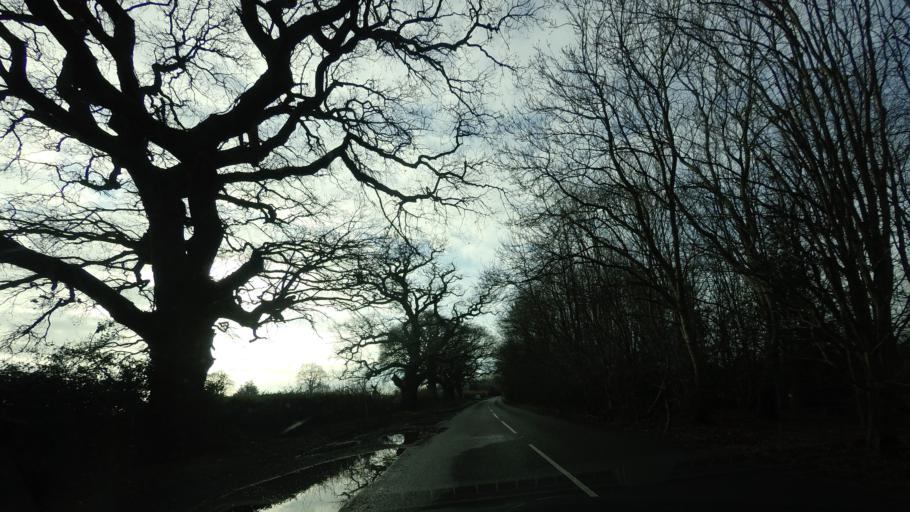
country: GB
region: England
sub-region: East Sussex
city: Battle
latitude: 50.9074
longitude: 0.4833
